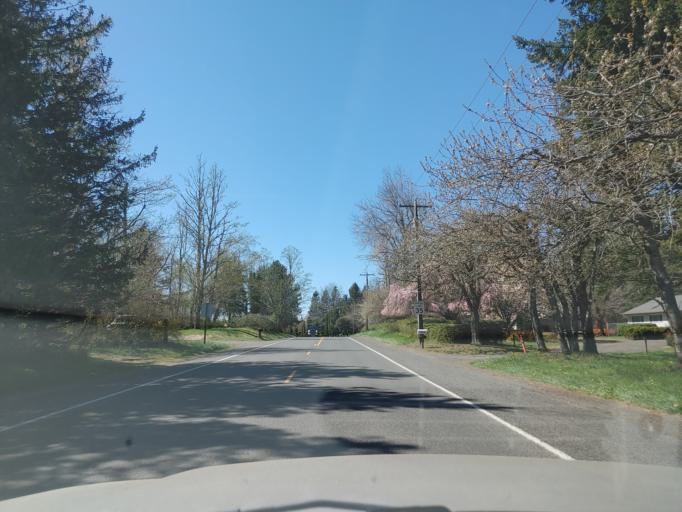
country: US
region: Washington
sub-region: Clark County
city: Washougal
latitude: 45.5323
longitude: -122.2862
